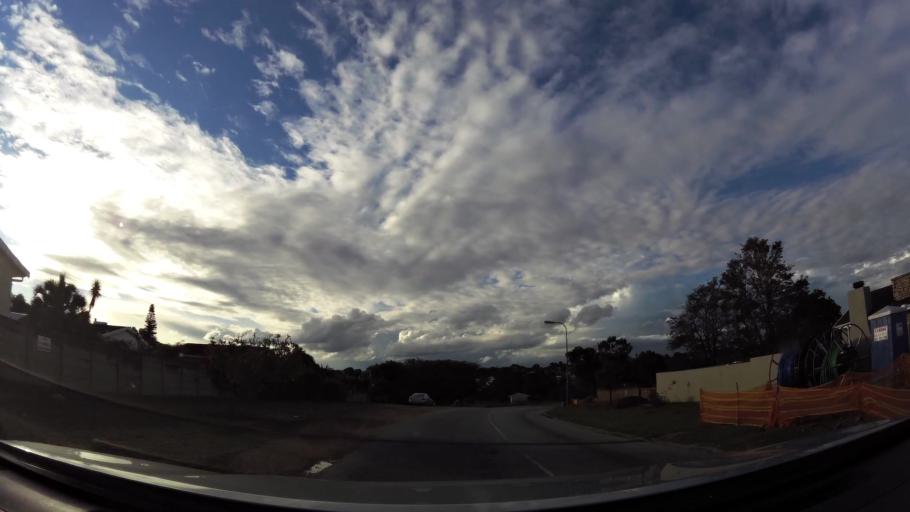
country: ZA
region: Eastern Cape
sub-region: Nelson Mandela Bay Metropolitan Municipality
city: Port Elizabeth
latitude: -33.9555
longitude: 25.5045
